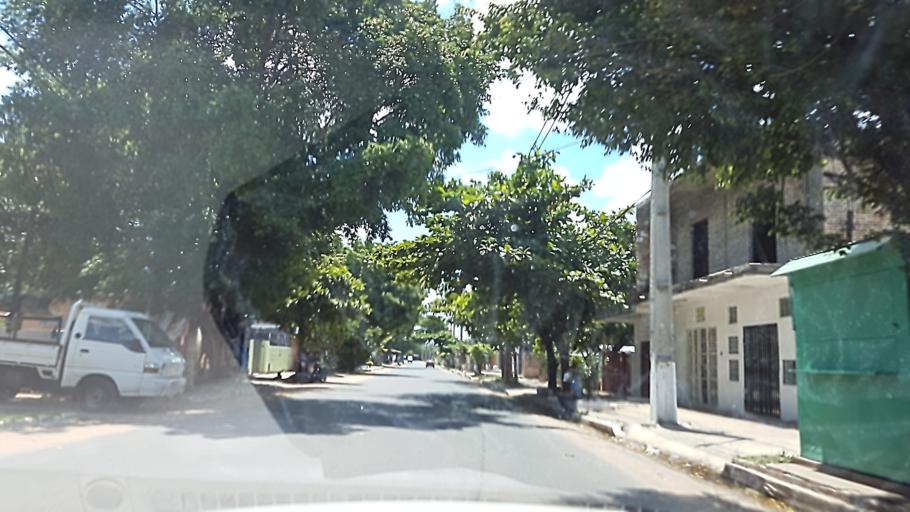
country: PY
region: Central
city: Colonia Mariano Roque Alonso
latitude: -25.2456
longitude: -57.5320
